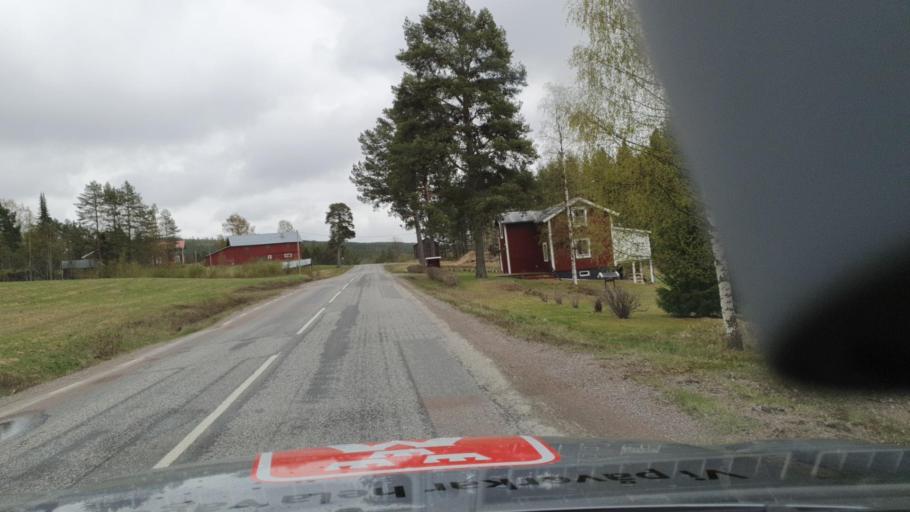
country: SE
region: Vaesterbotten
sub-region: Asele Kommun
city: Asele
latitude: 63.6905
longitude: 17.2373
